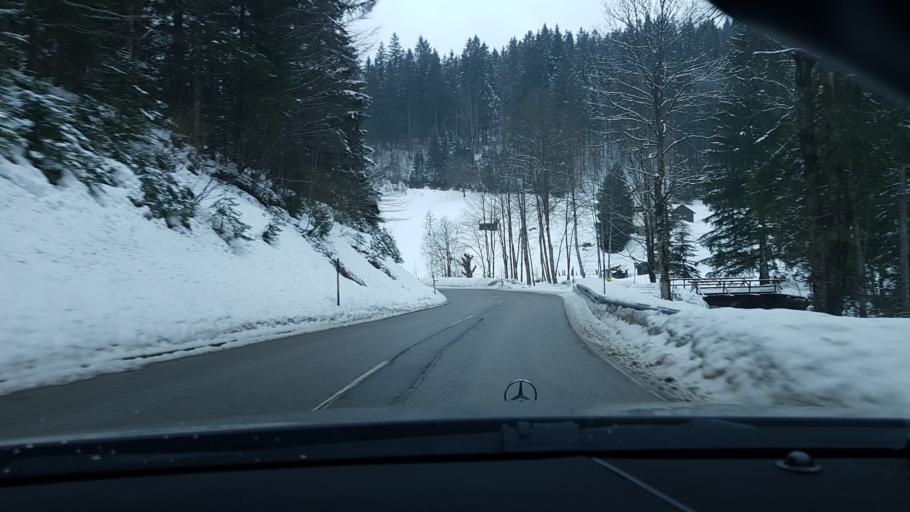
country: AT
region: Lower Austria
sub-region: Politischer Bezirk Scheibbs
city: Gaming
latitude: 47.8699
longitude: 15.1210
